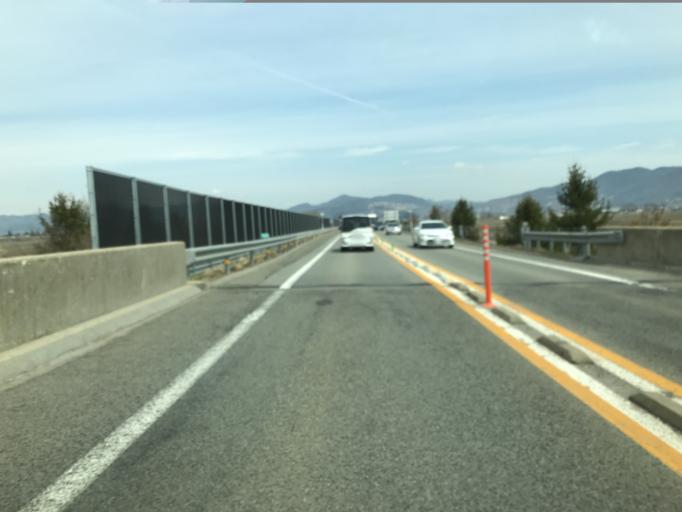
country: JP
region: Yamagata
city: Takahata
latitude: 38.0123
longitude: 140.1572
